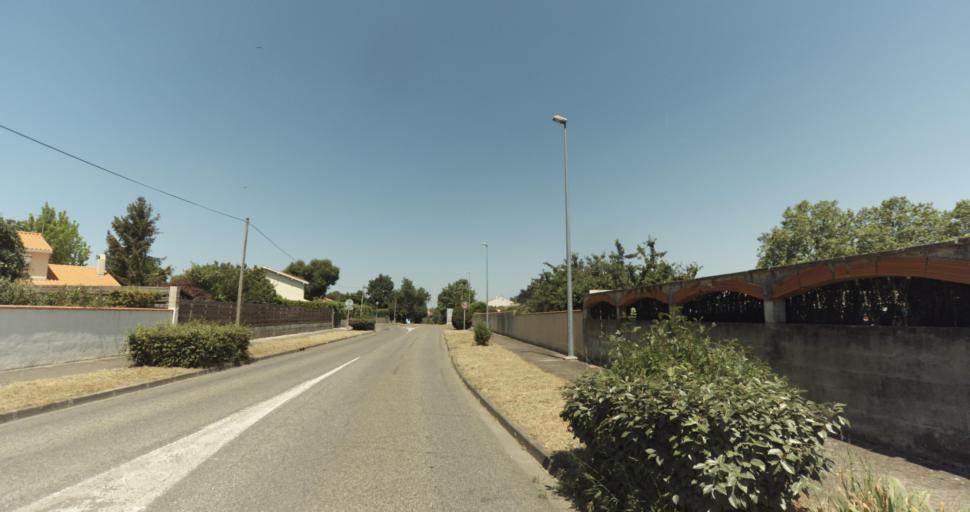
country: FR
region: Midi-Pyrenees
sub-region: Departement de la Haute-Garonne
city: Leguevin
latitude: 43.5931
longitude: 1.2297
